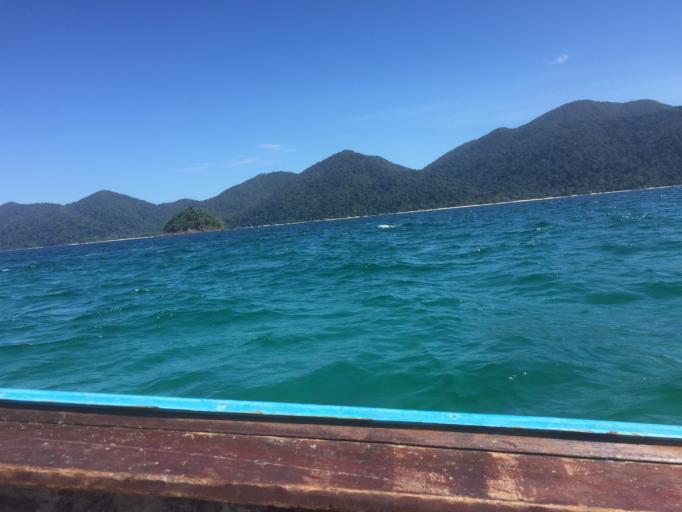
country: MY
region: Kedah
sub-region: Langkawi
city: Kuah
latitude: 6.5152
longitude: 99.2638
